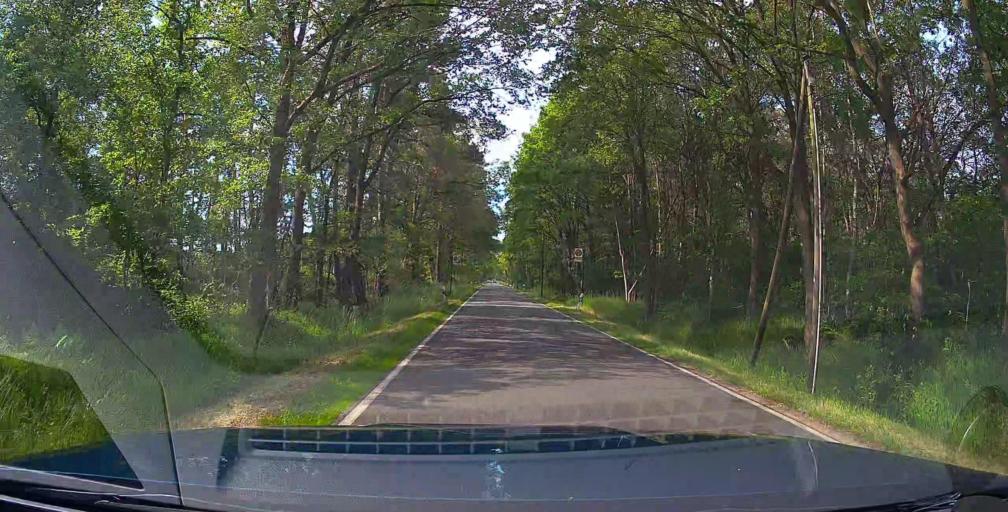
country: DE
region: North Rhine-Westphalia
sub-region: Regierungsbezirk Munster
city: Ladbergen
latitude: 52.1462
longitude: 7.8050
